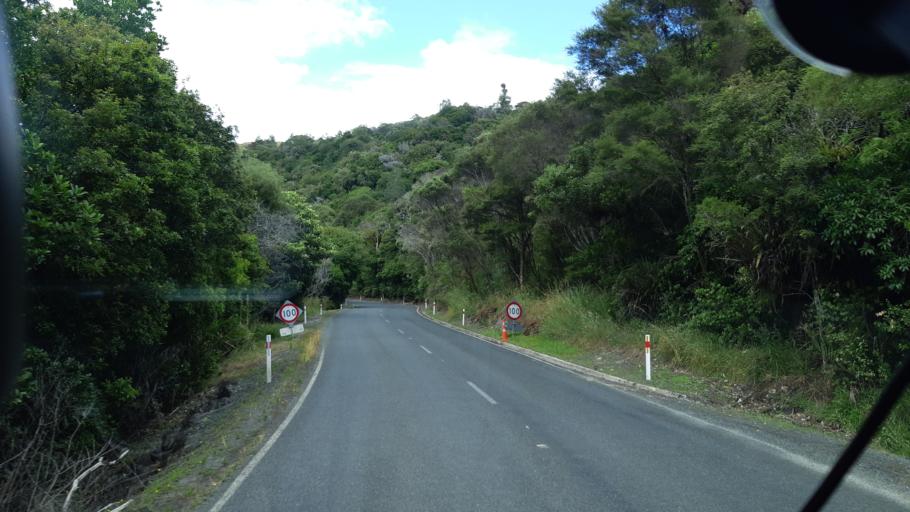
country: NZ
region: Northland
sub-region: Far North District
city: Taipa
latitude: -35.2464
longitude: 173.5337
